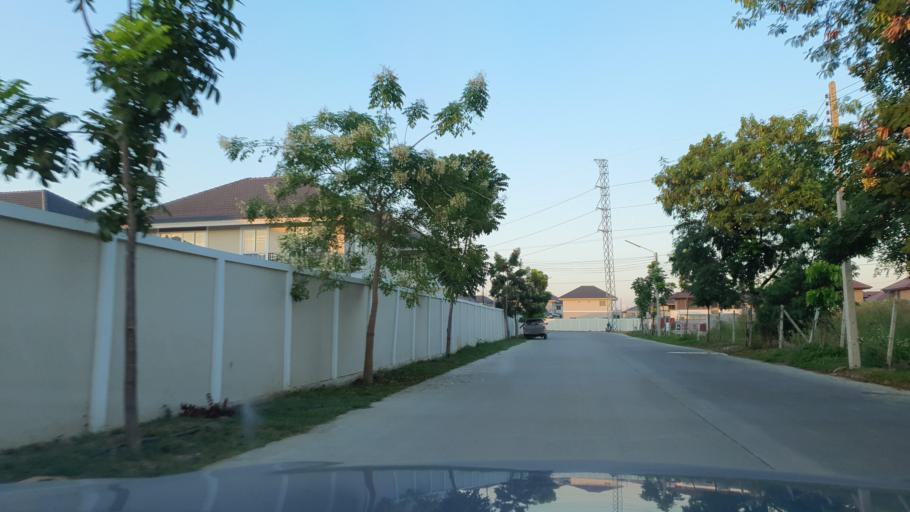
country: TH
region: Chiang Mai
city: Saraphi
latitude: 18.7262
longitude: 99.0764
